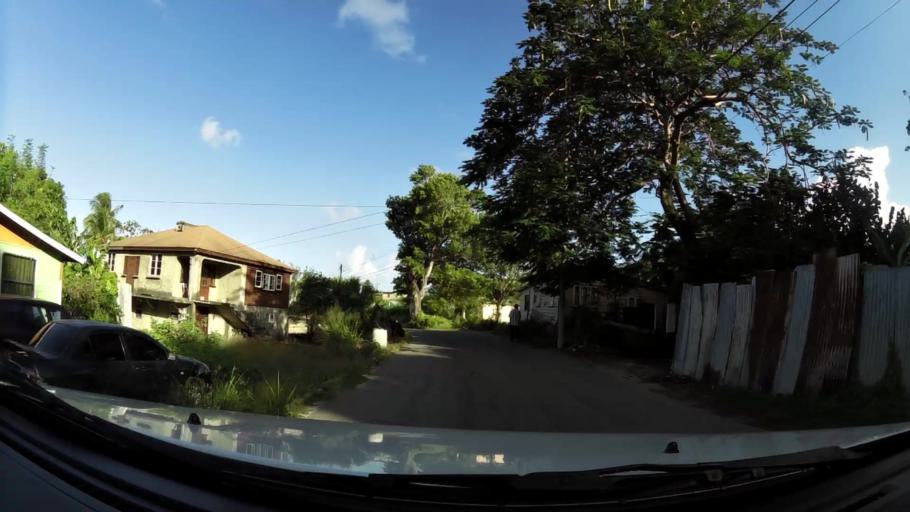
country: BB
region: Saint Michael
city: Bridgetown
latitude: 13.0920
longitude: -59.5929
